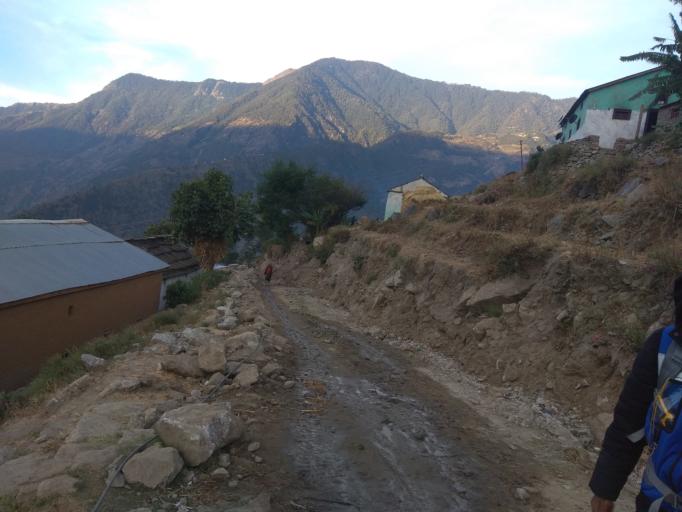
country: NP
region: Far Western
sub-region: Seti Zone
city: Achham
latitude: 29.2311
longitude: 81.6401
